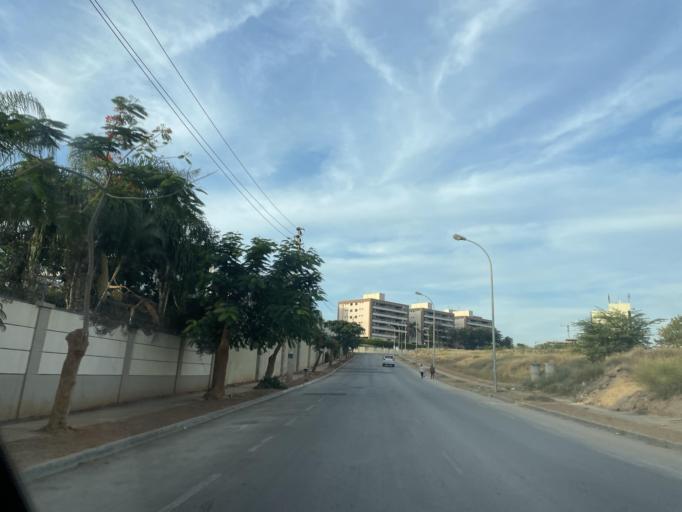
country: AO
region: Luanda
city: Luanda
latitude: -8.9290
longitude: 13.1873
